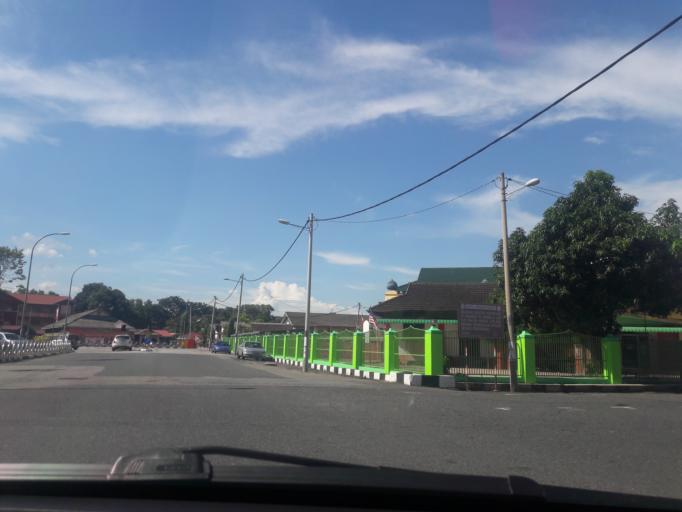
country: MY
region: Kedah
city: Sungai Petani
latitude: 5.6403
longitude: 100.4848
